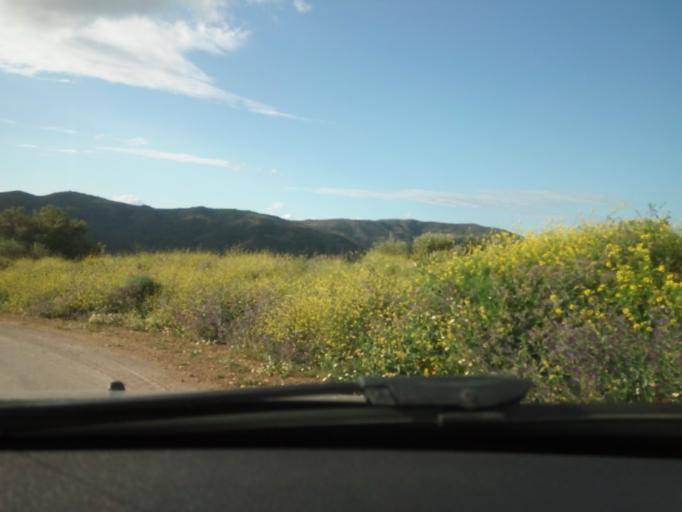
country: DZ
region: Tipaza
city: El Affroun
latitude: 36.3737
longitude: 2.5041
